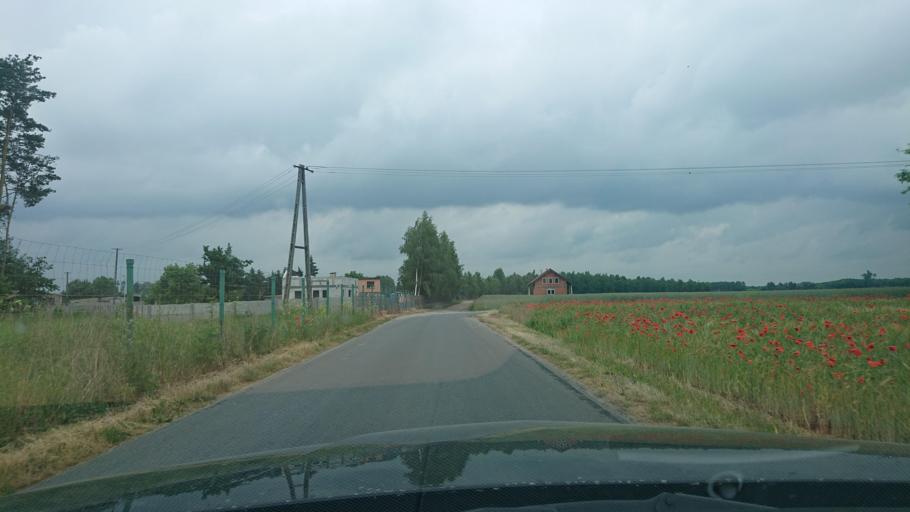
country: PL
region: Greater Poland Voivodeship
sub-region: Powiat gnieznienski
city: Gniezno
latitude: 52.4809
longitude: 17.5390
